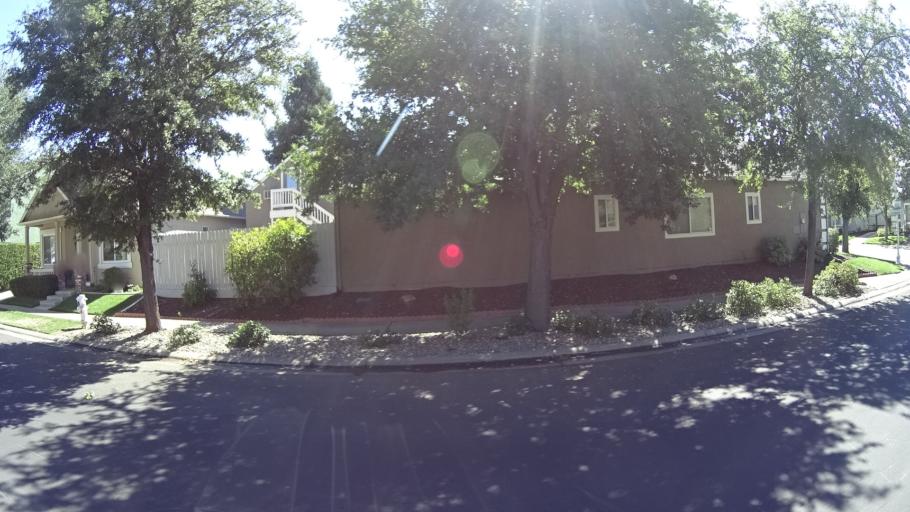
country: US
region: California
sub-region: Sacramento County
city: Laguna
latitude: 38.4171
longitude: -121.4653
